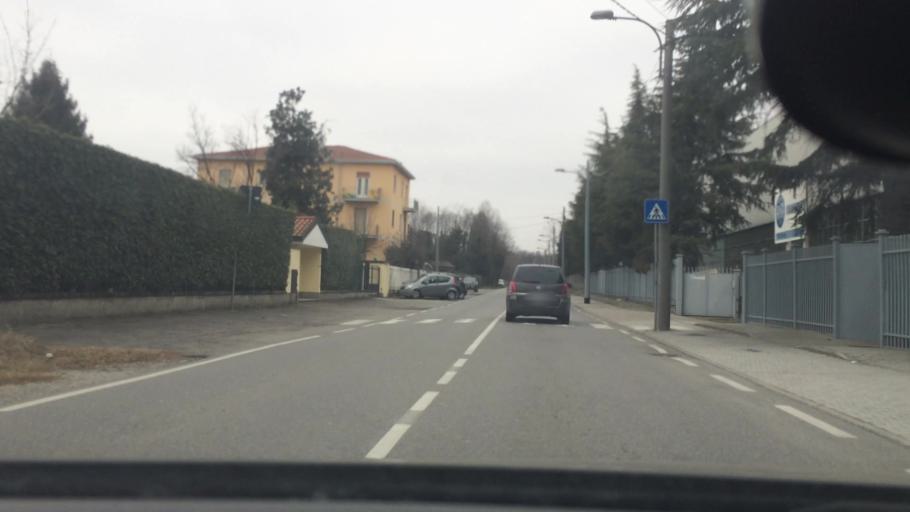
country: IT
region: Lombardy
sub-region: Provincia di Monza e Brianza
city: Villaggio del Sole
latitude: 45.6403
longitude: 9.1050
